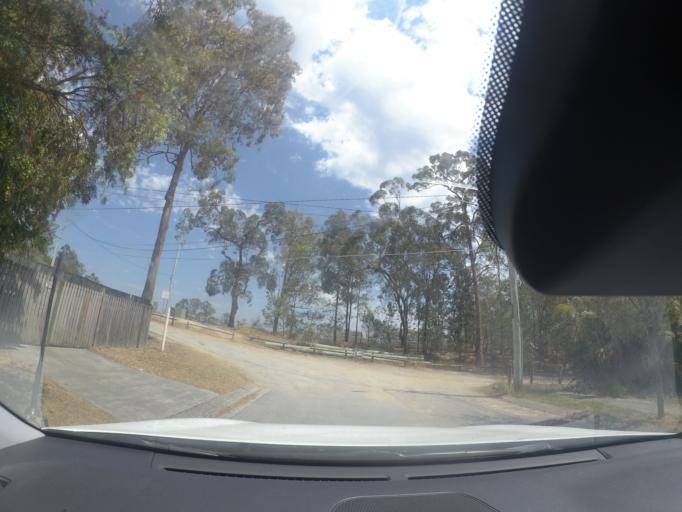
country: AU
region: Queensland
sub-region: Logan
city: Woodridge
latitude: -27.6186
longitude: 153.0976
